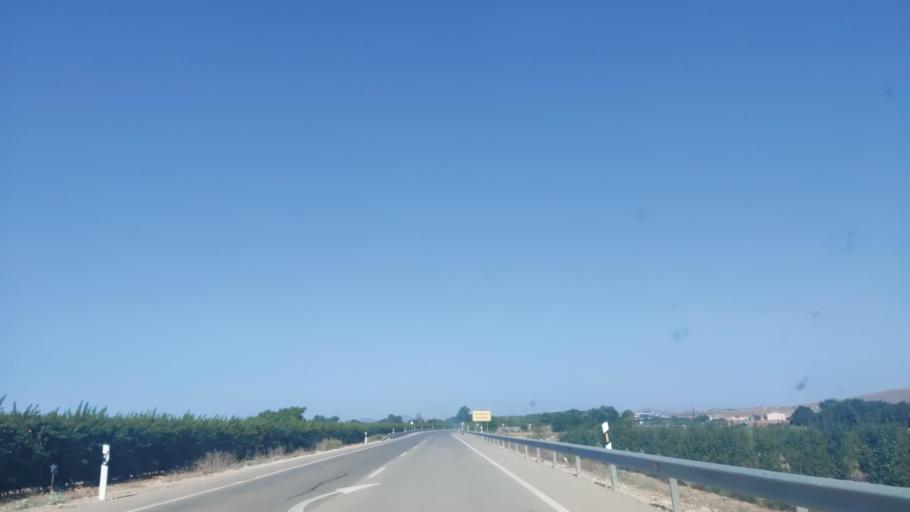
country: ES
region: Castille-La Mancha
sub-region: Provincia de Albacete
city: Hellin
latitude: 38.4926
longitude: -1.6358
